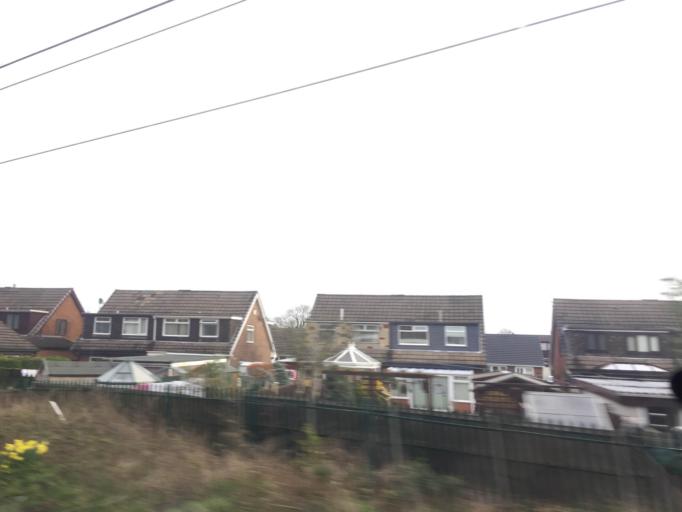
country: GB
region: England
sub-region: Lancashire
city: Coppull
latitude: 53.6288
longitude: -2.6613
